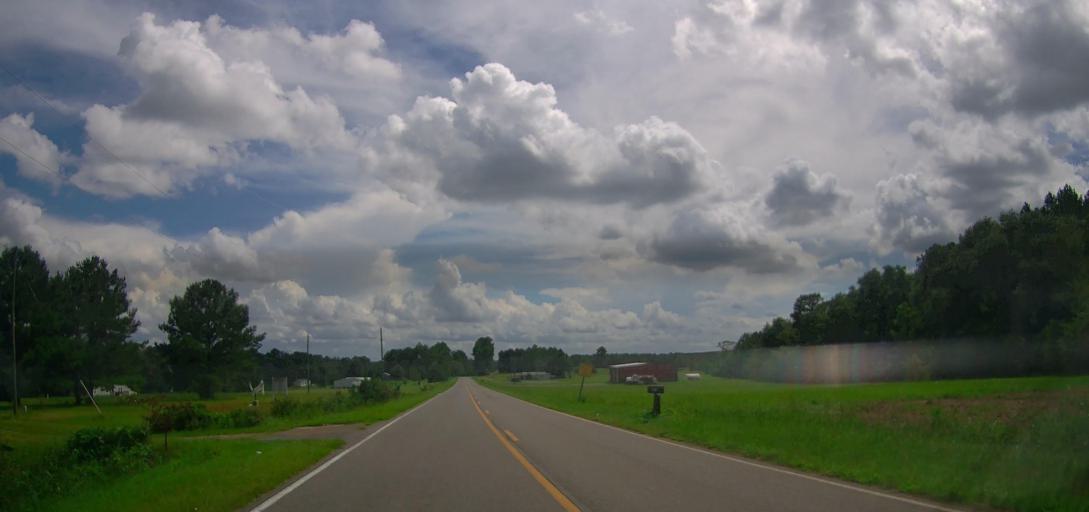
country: US
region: Georgia
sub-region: Taylor County
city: Butler
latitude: 32.4691
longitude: -84.2004
